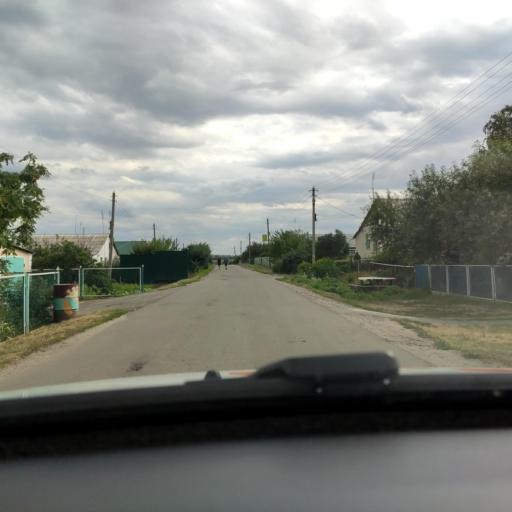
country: RU
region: Voronezj
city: Orlovo
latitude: 51.6540
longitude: 39.5721
